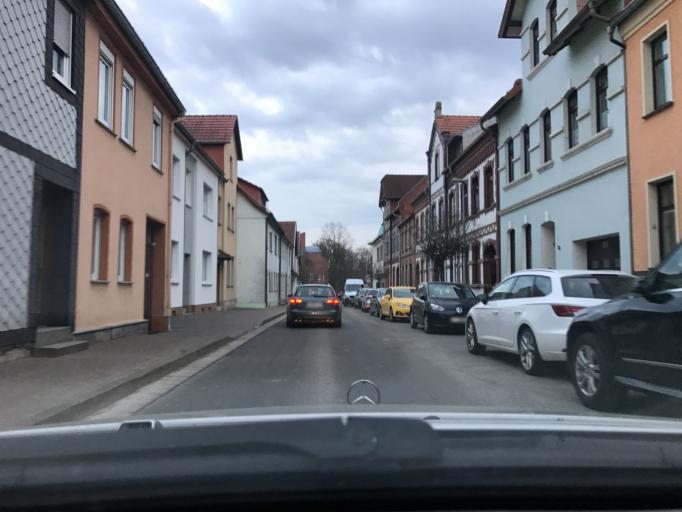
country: DE
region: Thuringia
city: Dingelstadt
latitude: 51.3161
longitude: 10.3118
